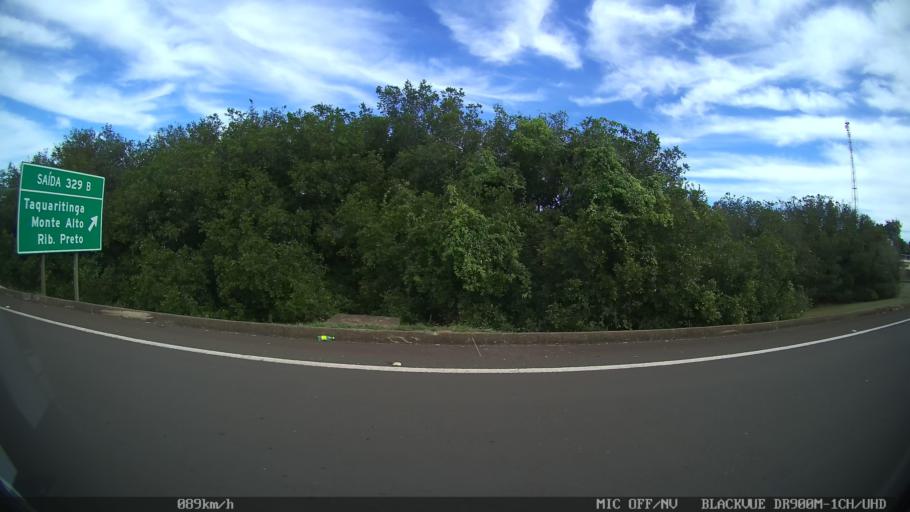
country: BR
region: Sao Paulo
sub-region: Taquaritinga
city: Taquaritinga
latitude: -21.4760
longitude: -48.5986
